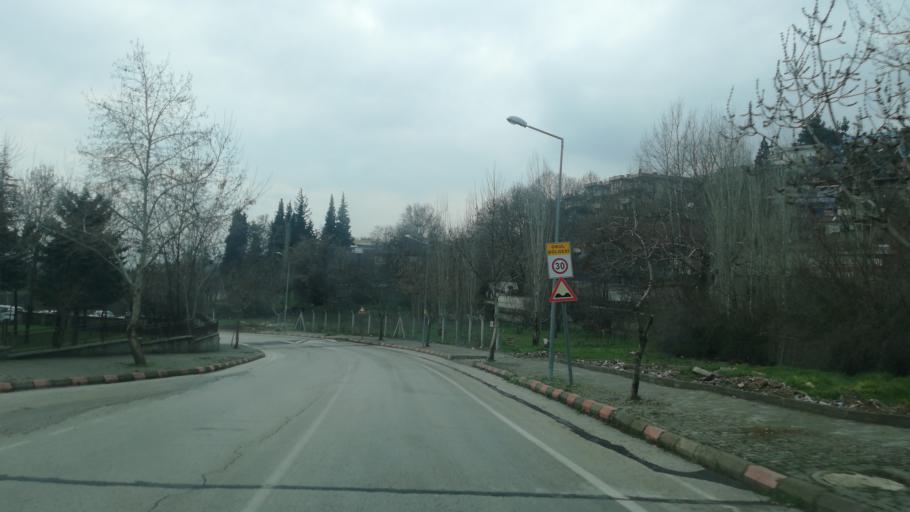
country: TR
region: Kahramanmaras
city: Kahramanmaras
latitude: 37.5942
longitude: 36.9364
